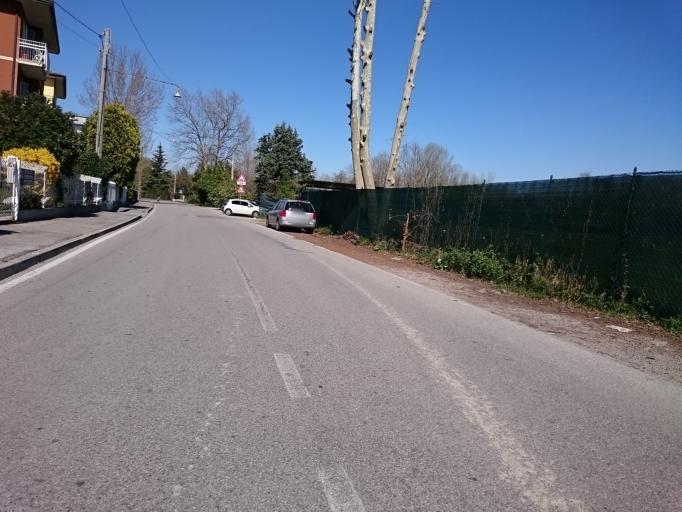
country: IT
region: Veneto
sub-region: Provincia di Padova
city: Padova
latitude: 45.3891
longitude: 11.9018
